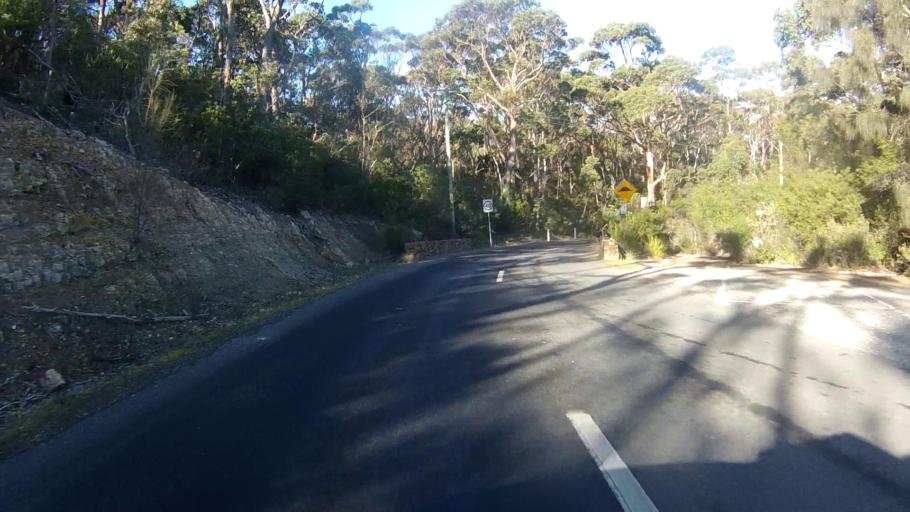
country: AU
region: Tasmania
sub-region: Clarence
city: Sandford
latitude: -43.0356
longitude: 147.9477
